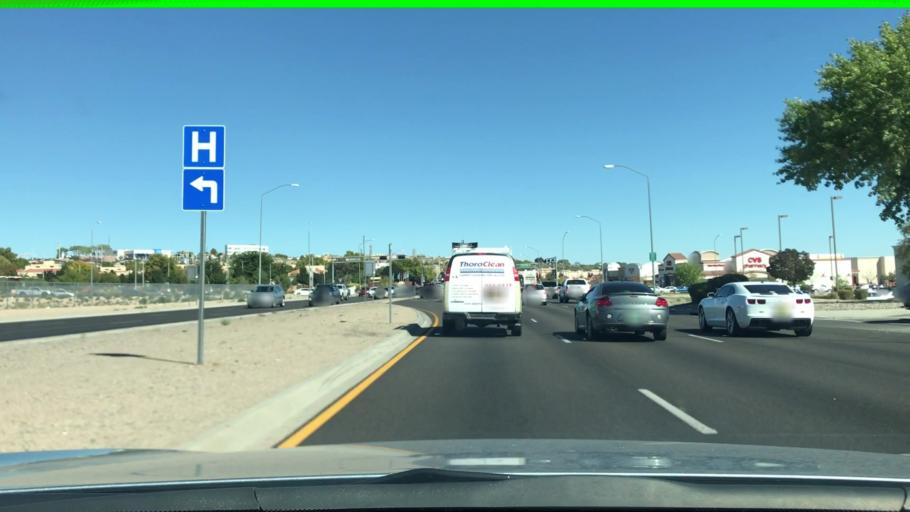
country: US
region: New Mexico
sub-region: Sandoval County
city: Rio Rancho
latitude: 35.2042
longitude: -106.6594
